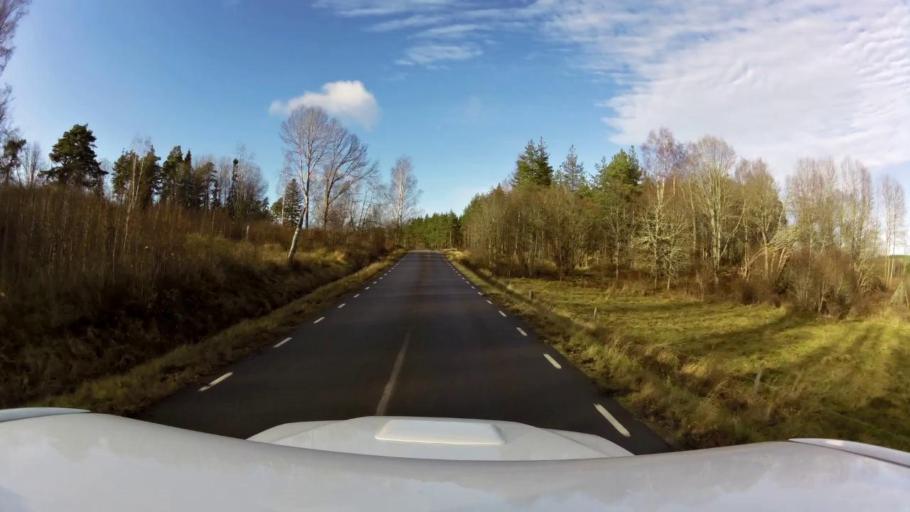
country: SE
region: OEstergoetland
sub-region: Linkopings Kommun
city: Sturefors
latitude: 58.3192
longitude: 15.6616
